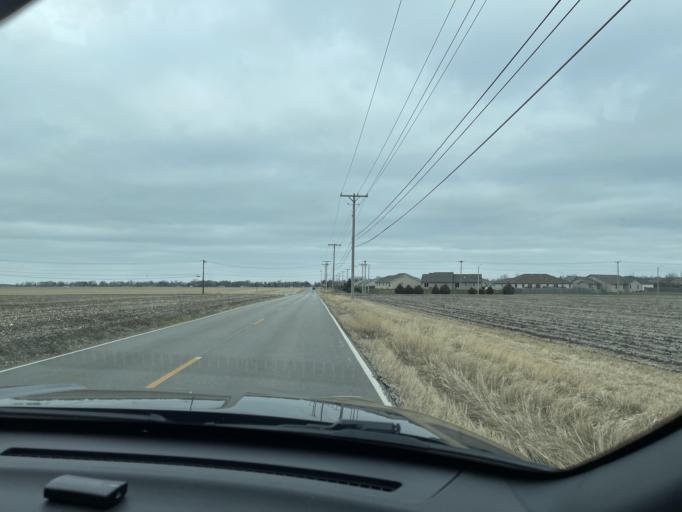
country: US
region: Illinois
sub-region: Sangamon County
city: Jerome
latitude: 39.7694
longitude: -89.7533
